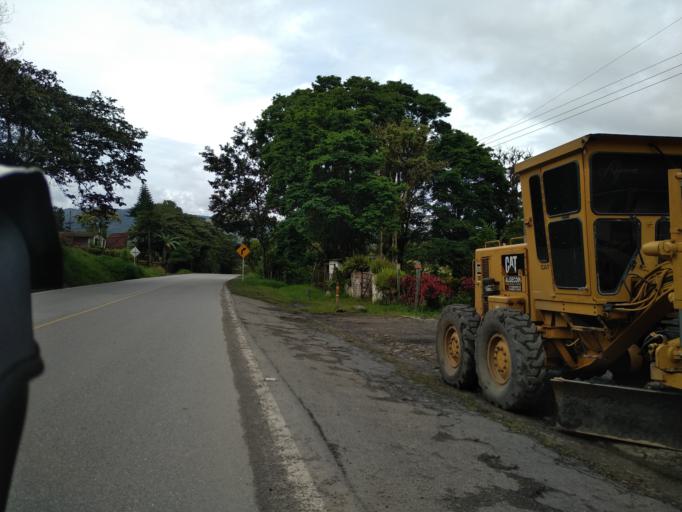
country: CO
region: Santander
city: Suaita
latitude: 6.1319
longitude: -73.3604
